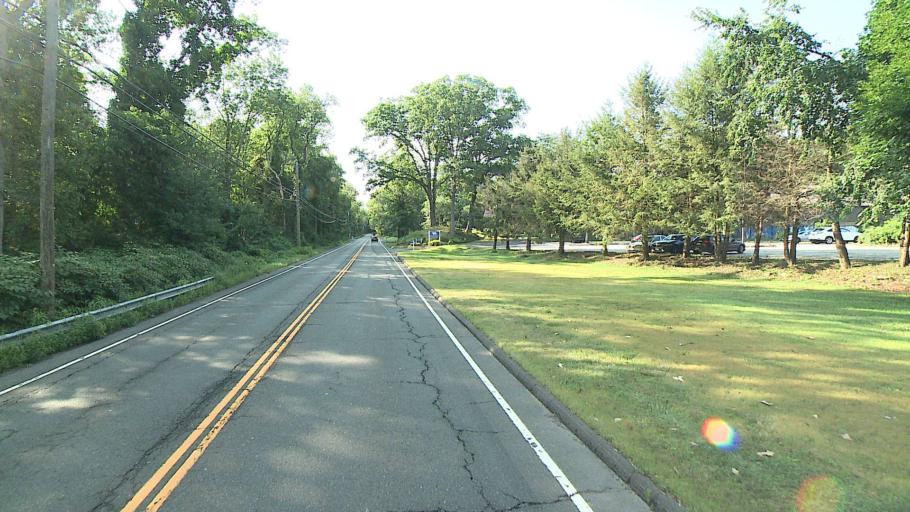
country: US
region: Connecticut
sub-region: Fairfield County
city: Georgetown
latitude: 41.2360
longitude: -73.4306
